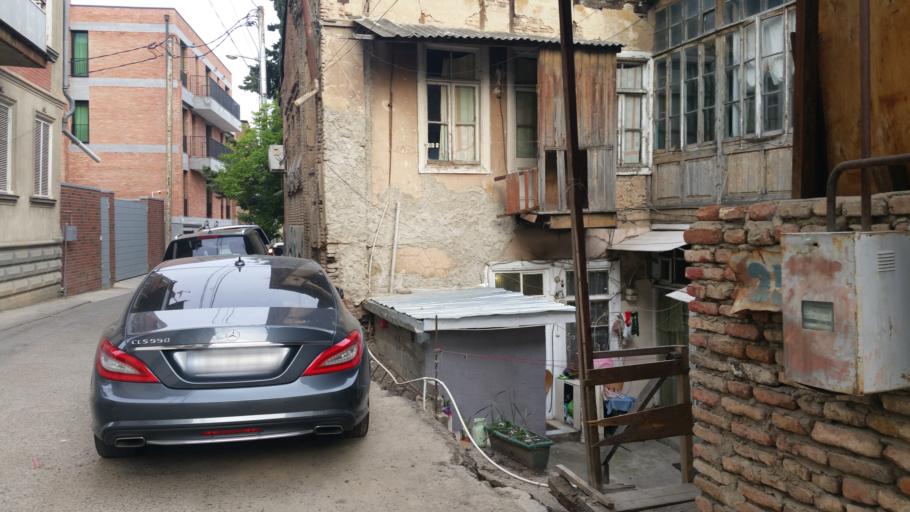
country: GE
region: T'bilisi
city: Tbilisi
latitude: 41.6905
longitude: 44.8152
